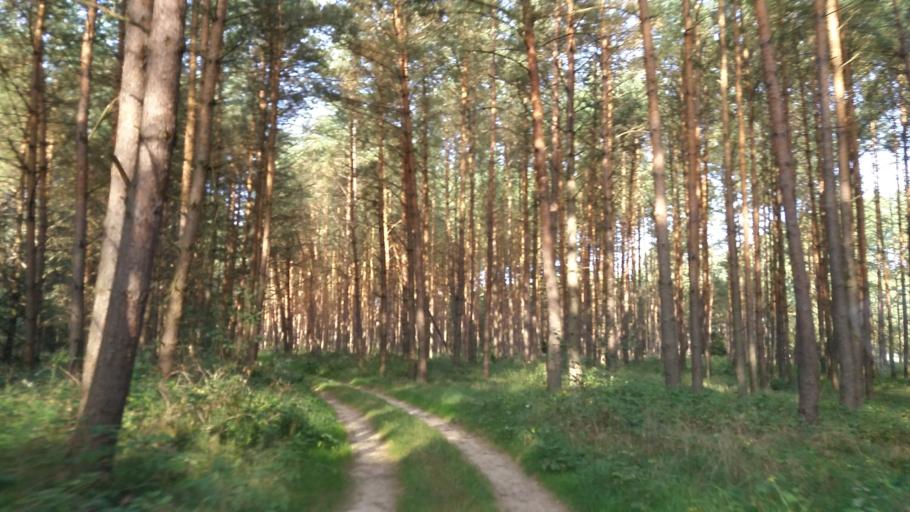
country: PL
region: West Pomeranian Voivodeship
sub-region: Powiat stargardzki
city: Suchan
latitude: 53.2447
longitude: 15.3730
